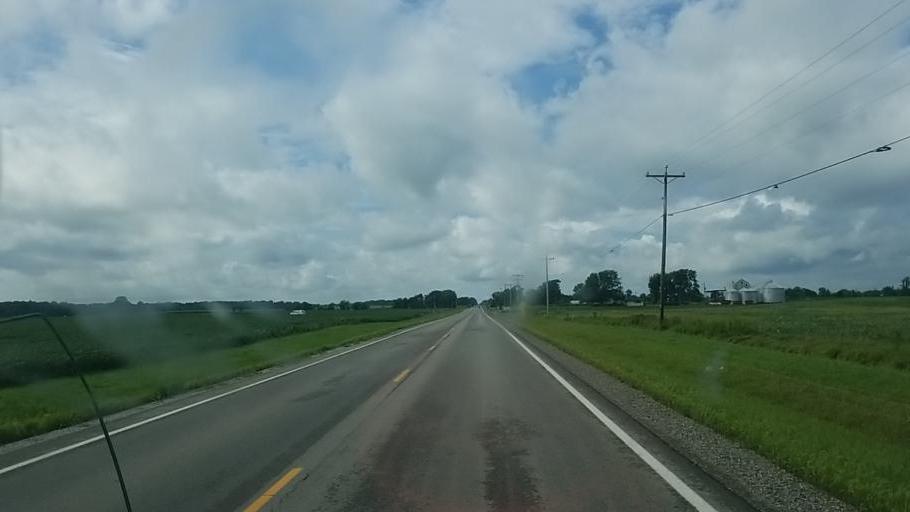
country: US
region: Ohio
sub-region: Hardin County
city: Kenton
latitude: 40.5610
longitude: -83.5430
